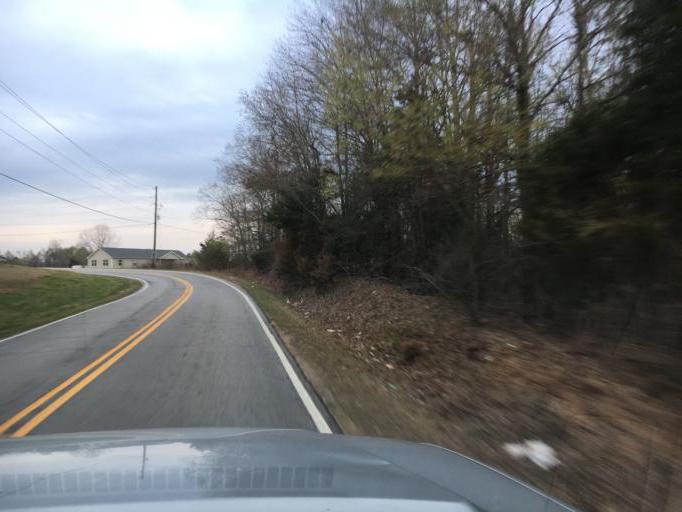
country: US
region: South Carolina
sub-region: Laurens County
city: Laurens
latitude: 34.5367
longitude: -82.0916
